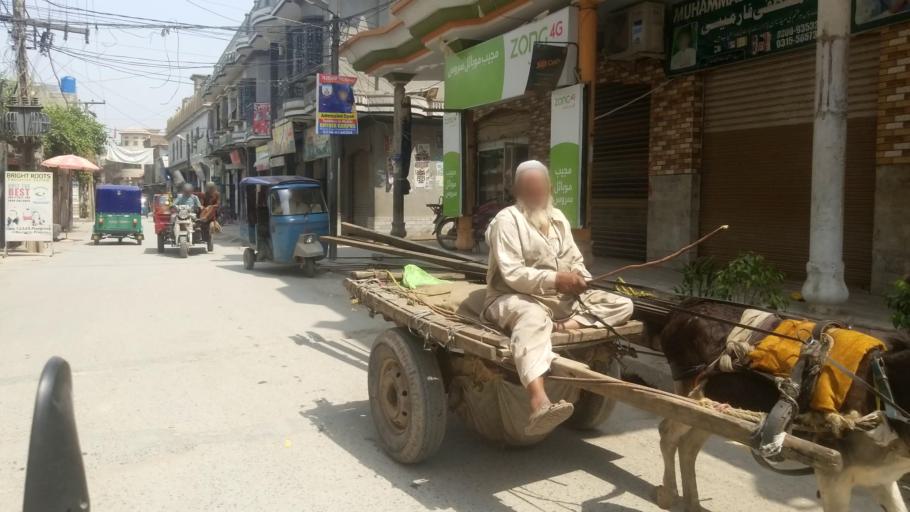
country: PK
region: Khyber Pakhtunkhwa
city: Peshawar
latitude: 34.0295
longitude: 71.5889
